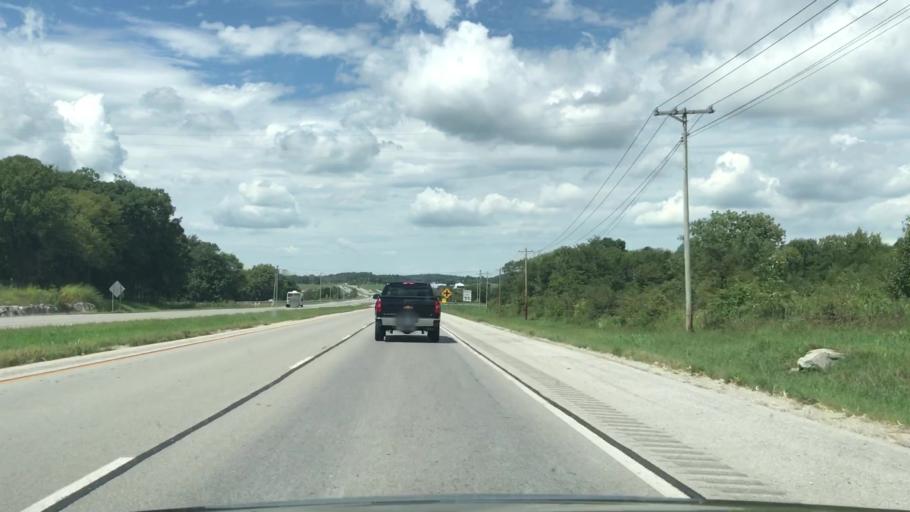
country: US
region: Kentucky
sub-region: Logan County
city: Russellville
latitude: 36.8658
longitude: -86.8700
